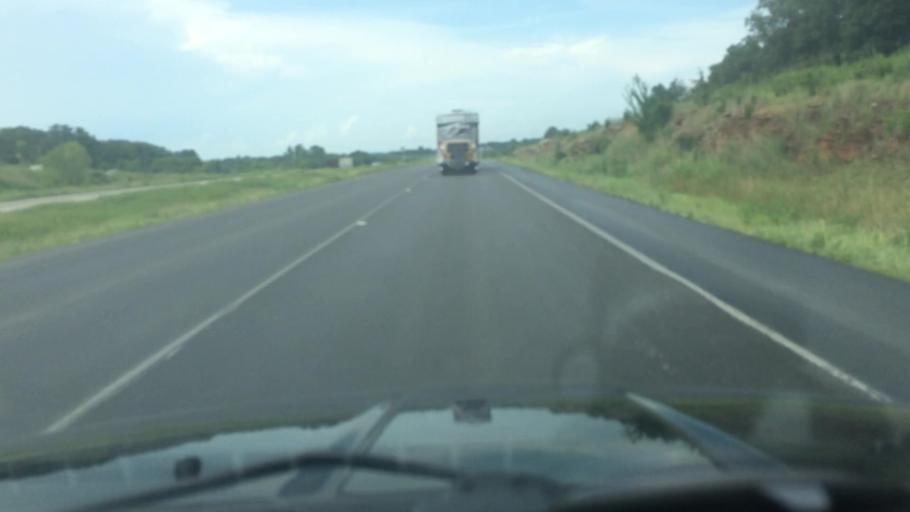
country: US
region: Missouri
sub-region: Saint Clair County
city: Osceola
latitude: 37.9807
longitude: -93.6492
